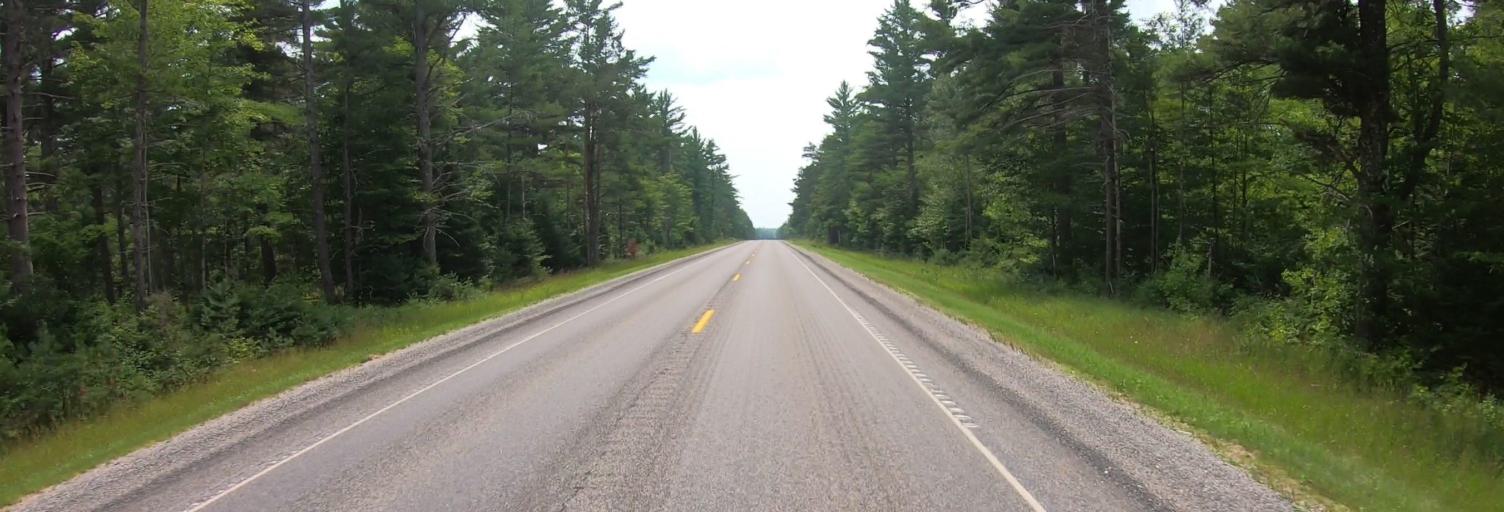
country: US
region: Michigan
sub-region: Alger County
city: Munising
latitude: 46.3473
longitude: -86.7274
